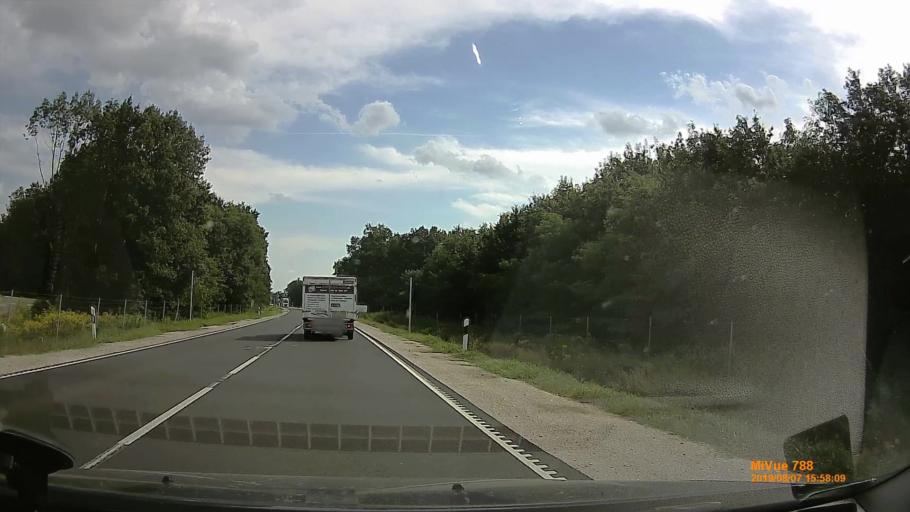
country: HU
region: Vas
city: Kormend
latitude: 47.0306
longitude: 16.6127
